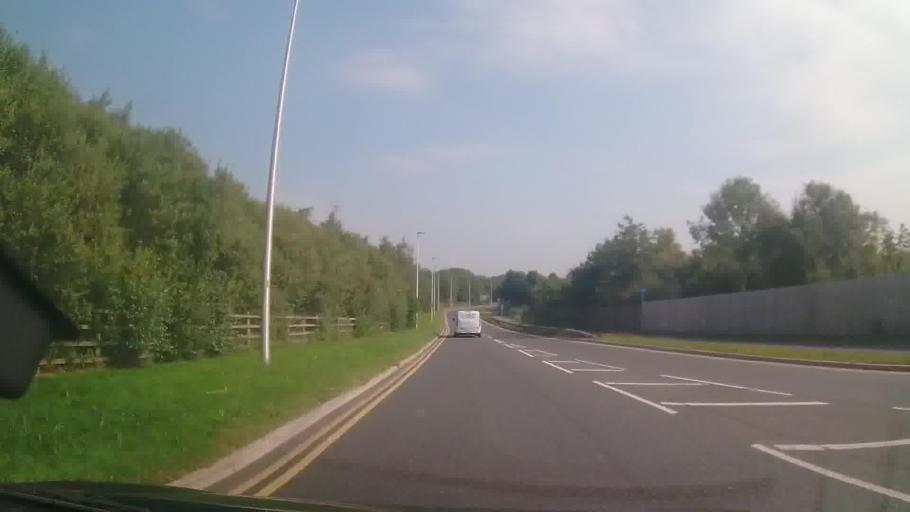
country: GB
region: England
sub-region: Warrington
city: Burtonwood
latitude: 53.4148
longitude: -2.6443
